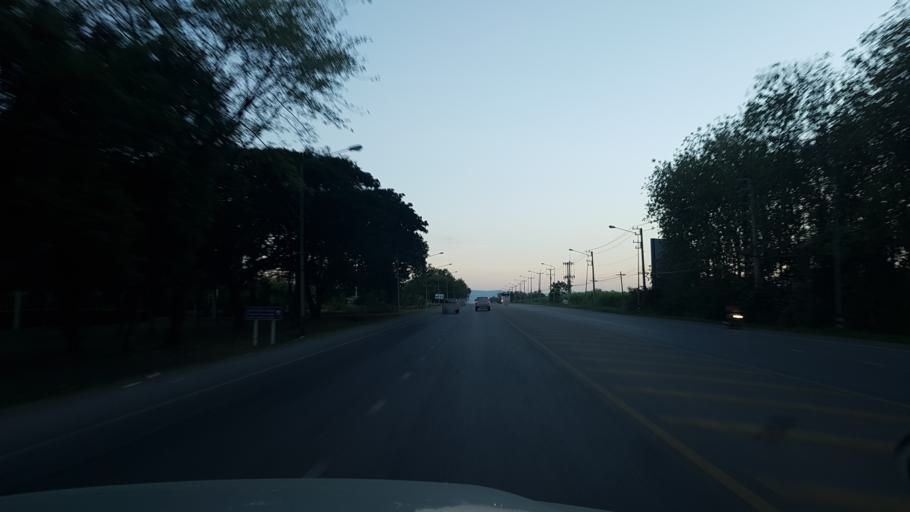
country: TH
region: Khon Kaen
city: Chum Phae
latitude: 16.4716
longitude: 102.1236
